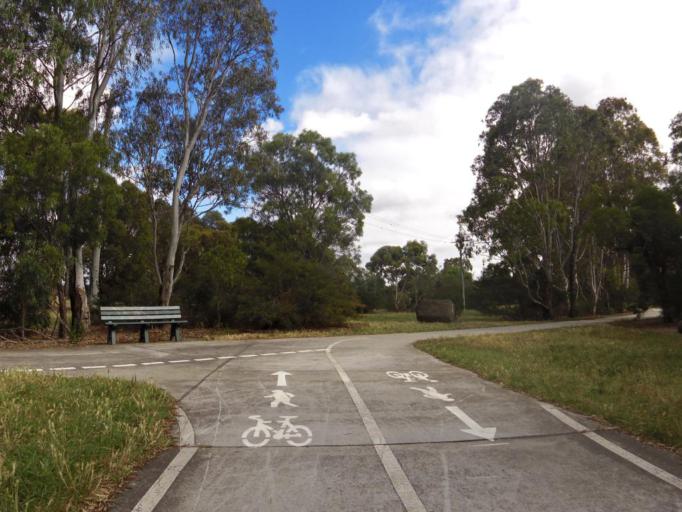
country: AU
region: Victoria
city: Heidelberg West
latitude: -37.7631
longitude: 145.0274
